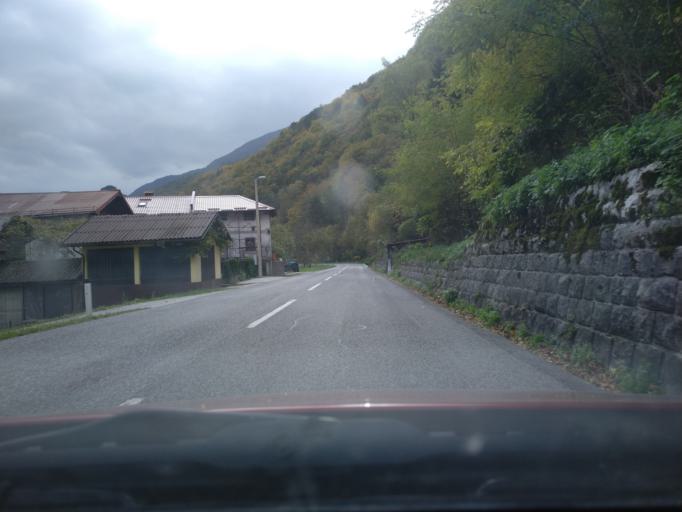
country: SI
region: Bovec
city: Bovec
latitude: 46.2903
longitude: 13.4993
